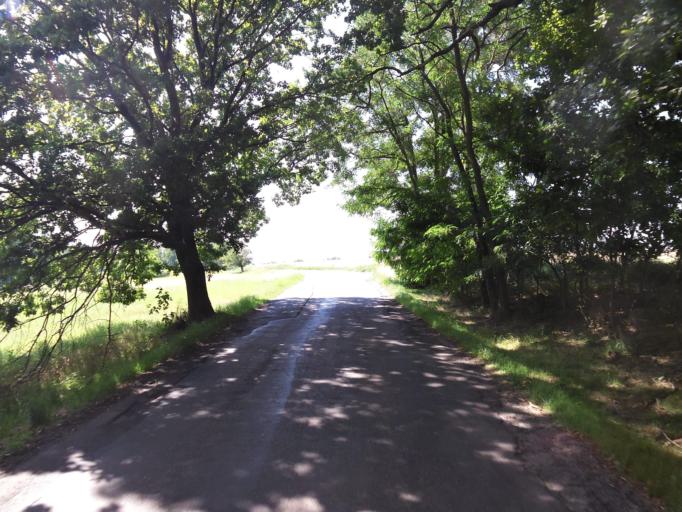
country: CZ
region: Central Bohemia
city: Cesky Brod
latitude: 50.0362
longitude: 14.8258
